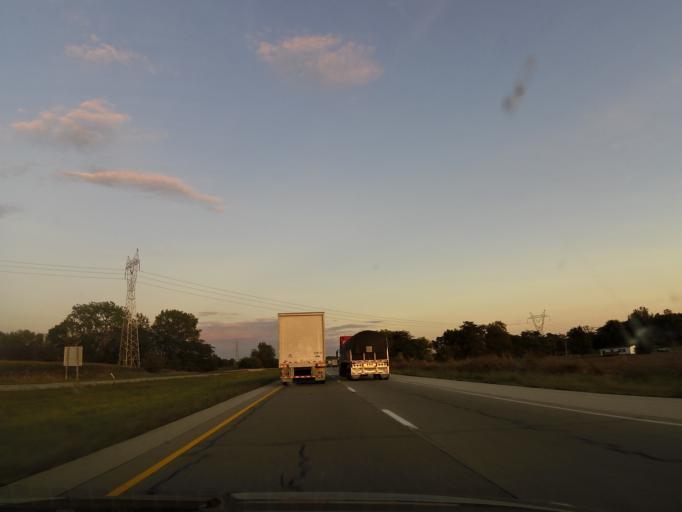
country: US
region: Indiana
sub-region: Shelby County
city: Shelbyville
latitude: 39.5217
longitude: -85.7273
